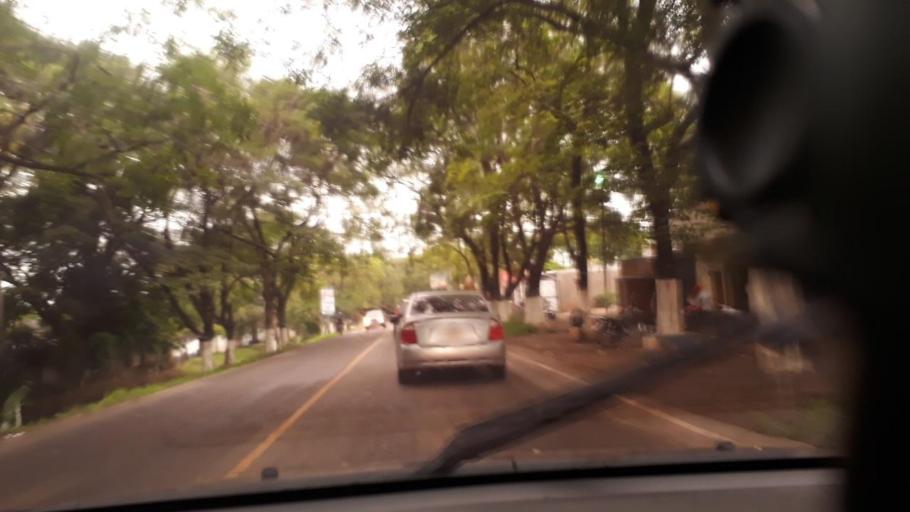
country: GT
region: Jutiapa
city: Asuncion Mita
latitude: 14.3423
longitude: -89.7141
